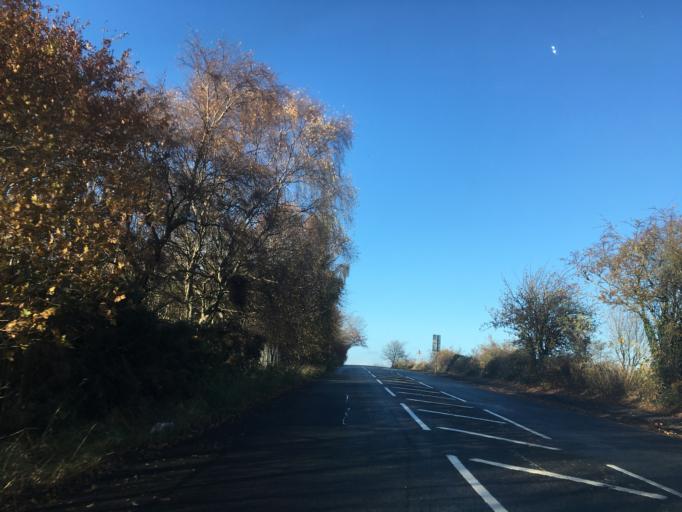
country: GB
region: Scotland
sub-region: Midlothian
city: Loanhead
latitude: 55.9143
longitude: -3.1797
